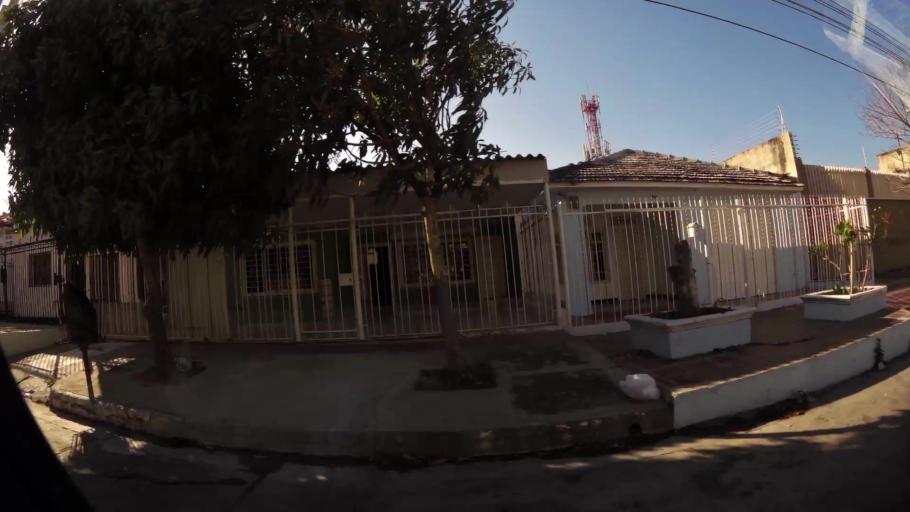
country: CO
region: Atlantico
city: Barranquilla
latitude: 10.9643
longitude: -74.7901
